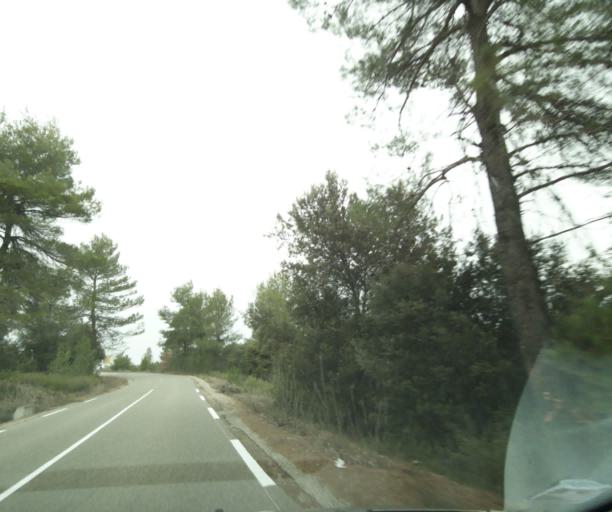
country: FR
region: Provence-Alpes-Cote d'Azur
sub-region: Departement du Vaucluse
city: Beaumont-de-Pertuis
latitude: 43.6896
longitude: 5.7358
